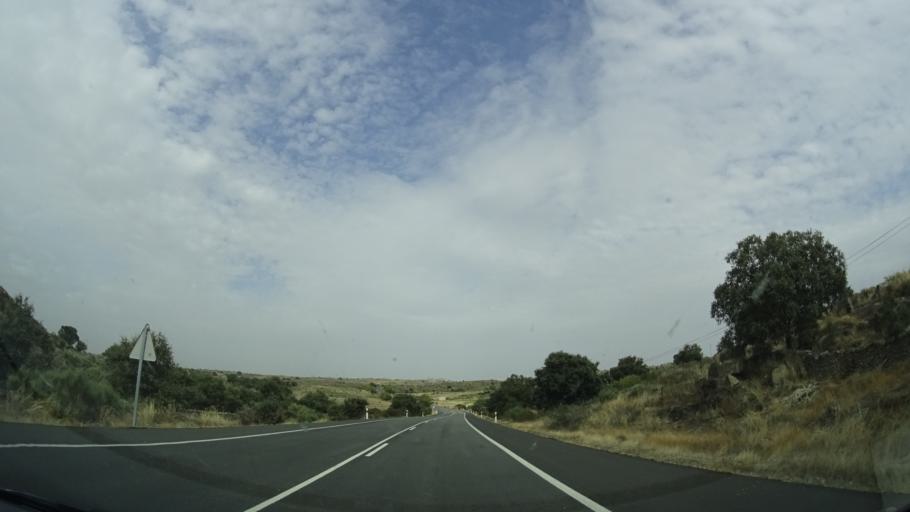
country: ES
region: Extremadura
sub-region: Provincia de Caceres
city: Trujillo
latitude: 39.4263
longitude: -5.8925
